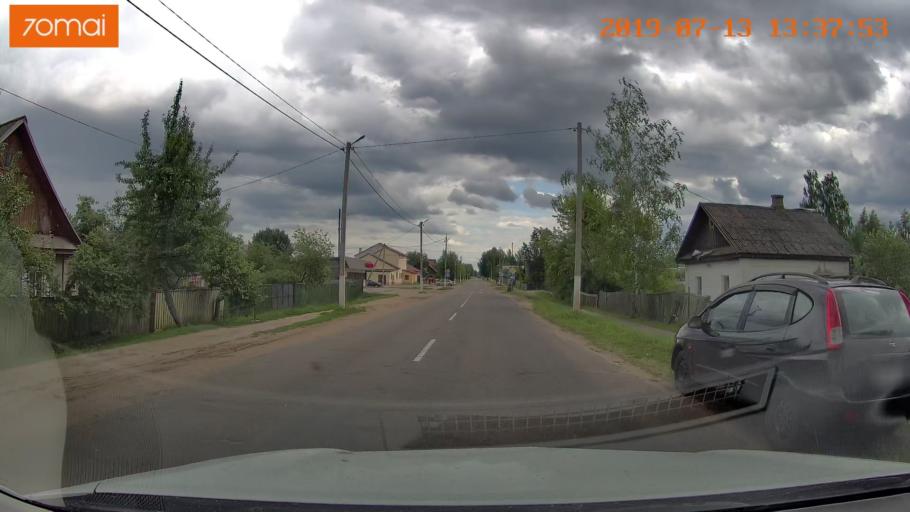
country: BY
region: Mogilev
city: Asipovichy
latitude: 53.2998
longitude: 28.6290
